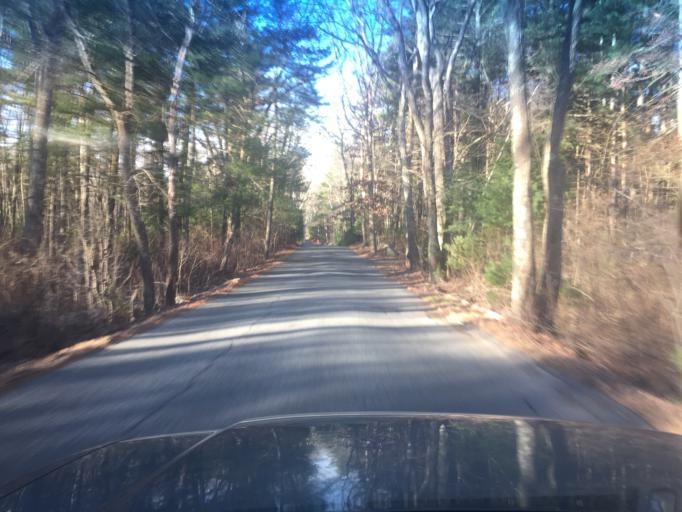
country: US
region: Massachusetts
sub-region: Middlesex County
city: Holliston
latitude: 42.2158
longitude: -71.4643
